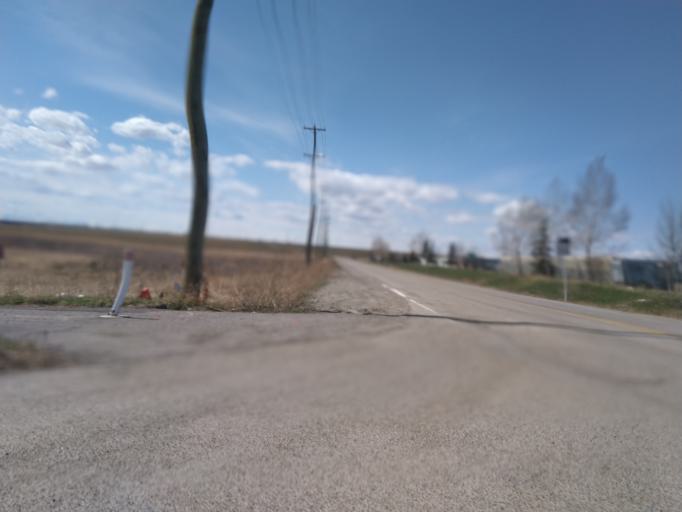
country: CA
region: Alberta
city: Chestermere
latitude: 50.9505
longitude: -113.9120
